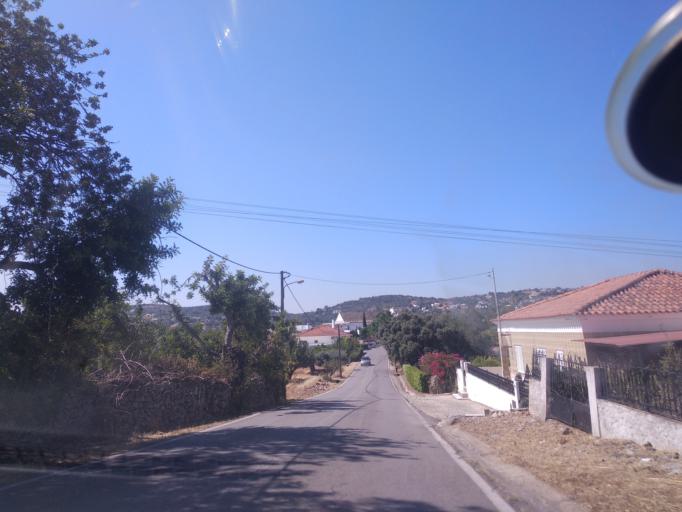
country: PT
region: Faro
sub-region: Sao Bras de Alportel
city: Sao Bras de Alportel
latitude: 37.1550
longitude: -7.9317
